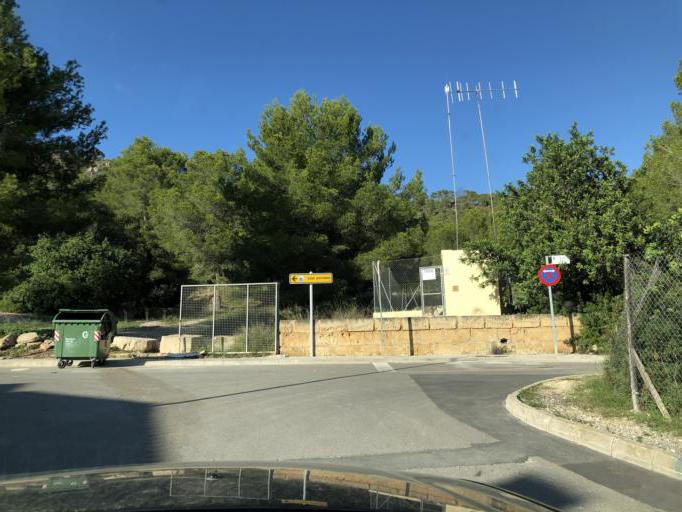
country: ES
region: Balearic Islands
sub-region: Illes Balears
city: Camp de Mar
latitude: 39.5402
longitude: 2.4392
